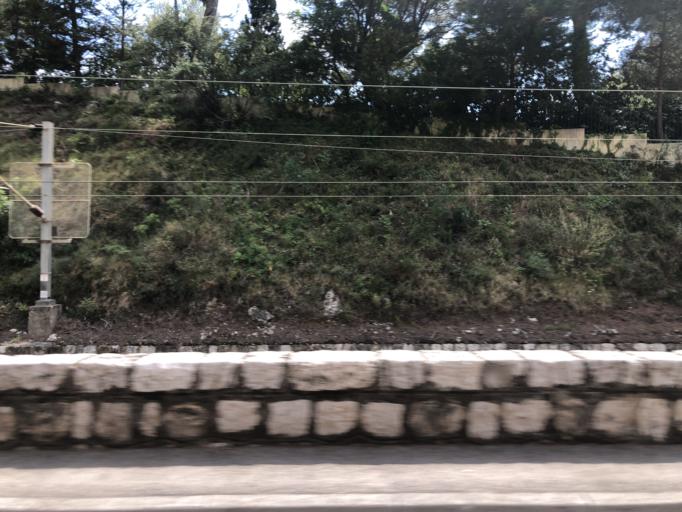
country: FR
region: Provence-Alpes-Cote d'Azur
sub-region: Departement des Alpes-Maritimes
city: Eze
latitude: 43.7229
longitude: 7.3616
